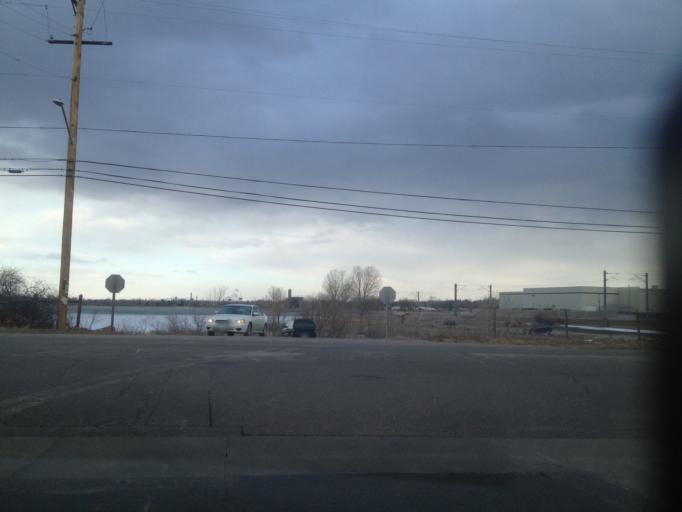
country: US
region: Colorado
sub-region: Adams County
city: Berkley
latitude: 39.8055
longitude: -105.0443
